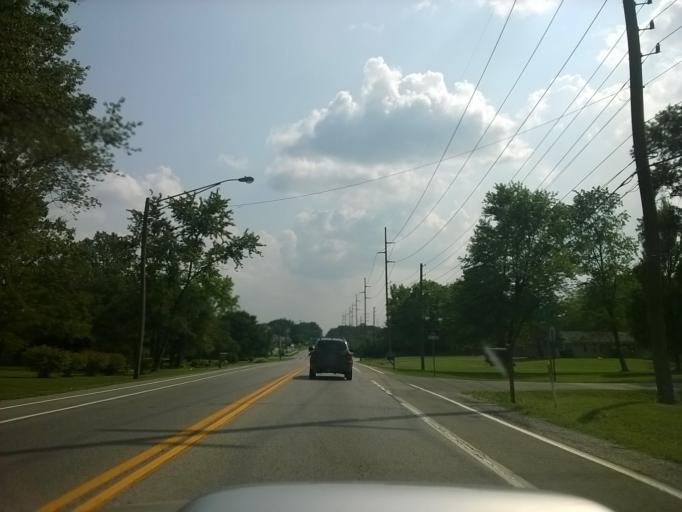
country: US
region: Indiana
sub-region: Marion County
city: Broad Ripple
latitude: 39.8718
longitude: -86.0955
